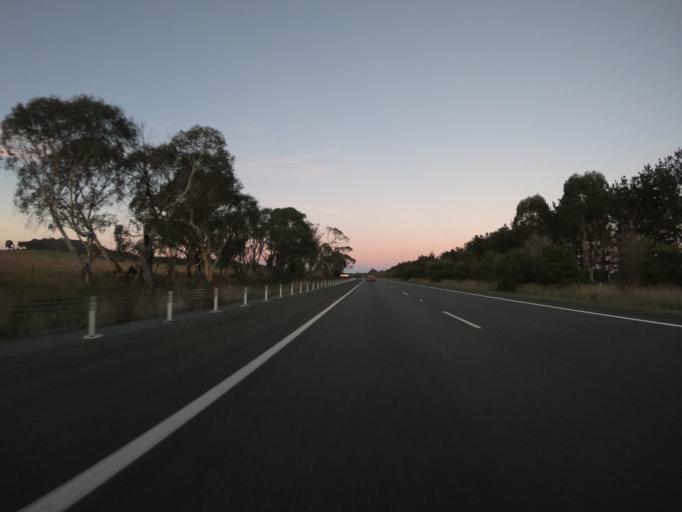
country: AU
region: New South Wales
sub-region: Wingecarribee
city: Bundanoon
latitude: -34.6555
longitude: 150.0843
